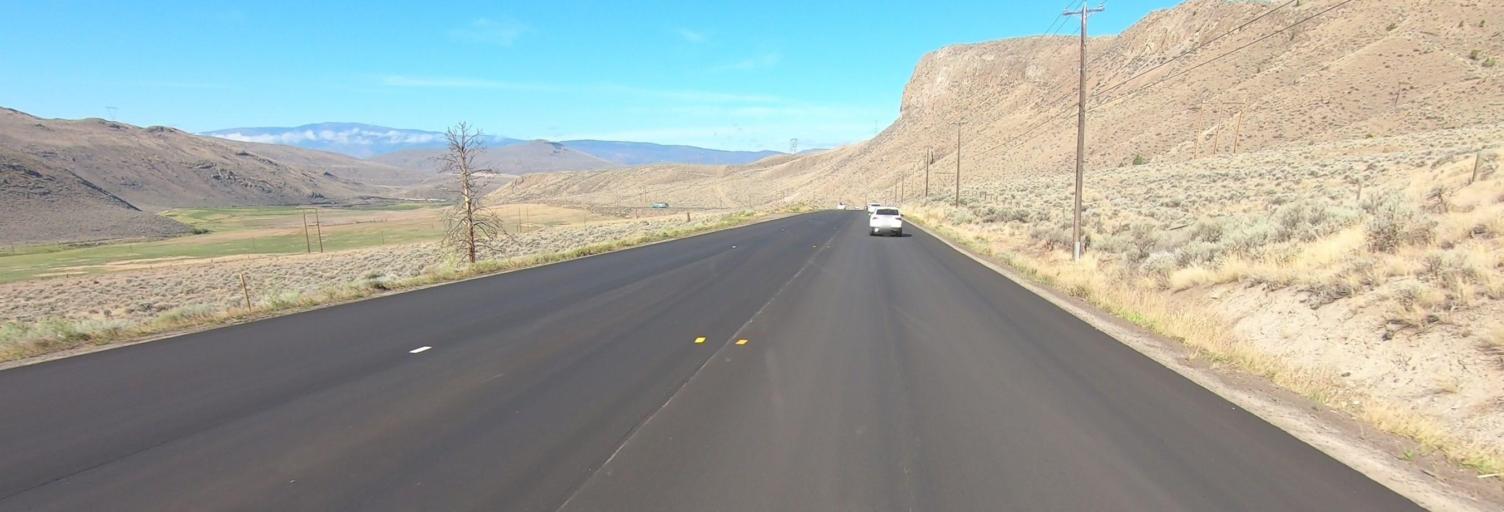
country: CA
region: British Columbia
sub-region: Thompson-Nicola Regional District
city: Ashcroft
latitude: 50.7903
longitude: -121.1684
